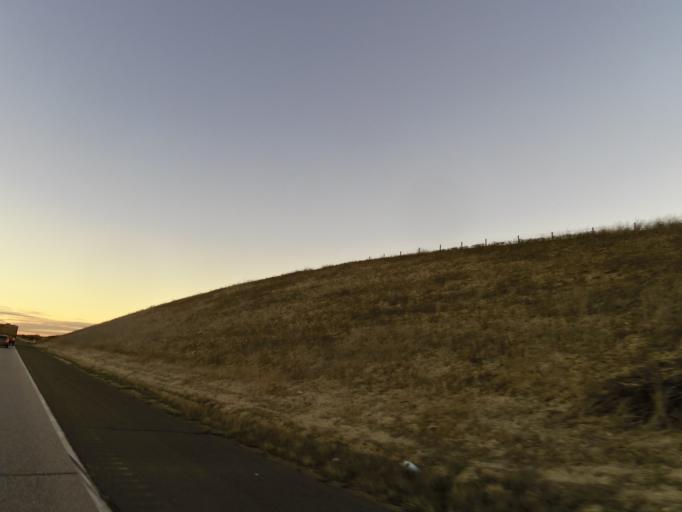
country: US
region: California
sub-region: Monterey County
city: King City
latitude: 36.0267
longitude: -120.9366
